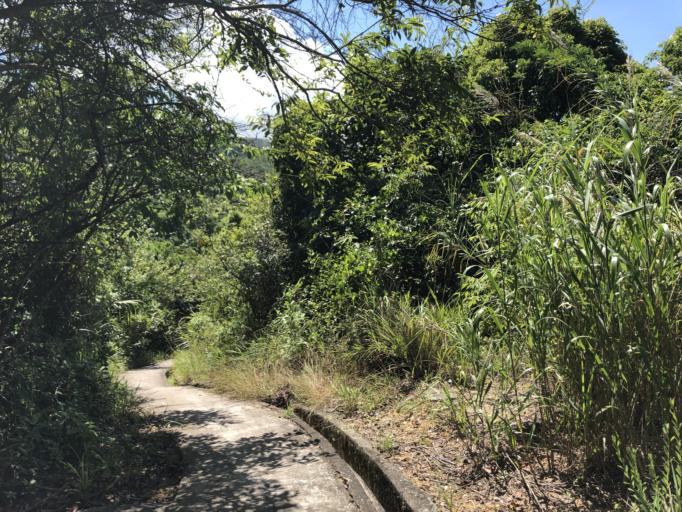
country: HK
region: Tuen Mun
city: Tuen Mun
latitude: 22.2888
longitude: 113.9804
